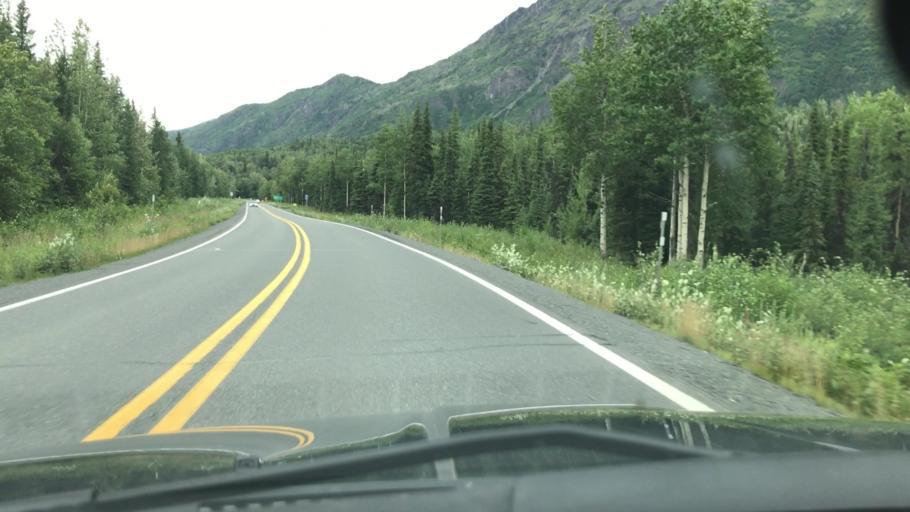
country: US
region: Alaska
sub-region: Kenai Peninsula Borough
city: Seward
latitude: 60.4864
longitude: -149.9652
